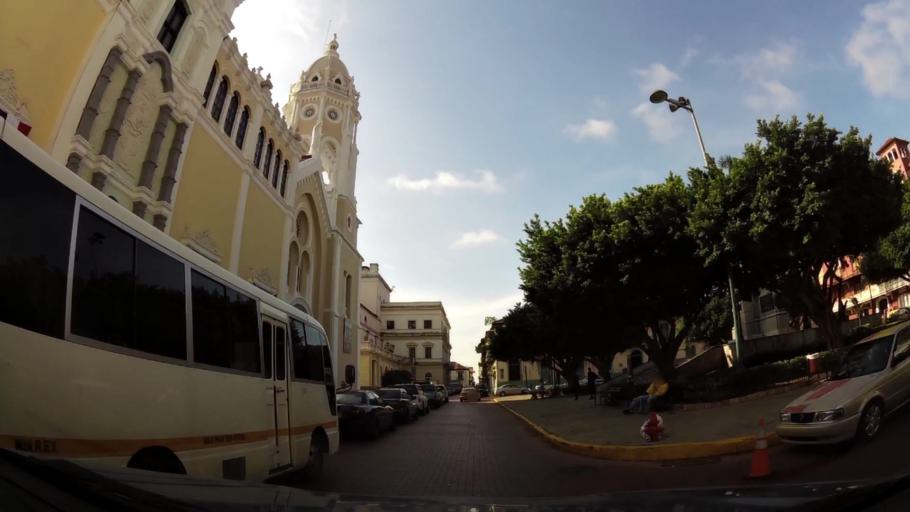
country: PA
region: Panama
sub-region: Distrito de Panama
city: Ancon
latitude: 8.9535
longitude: -79.5333
